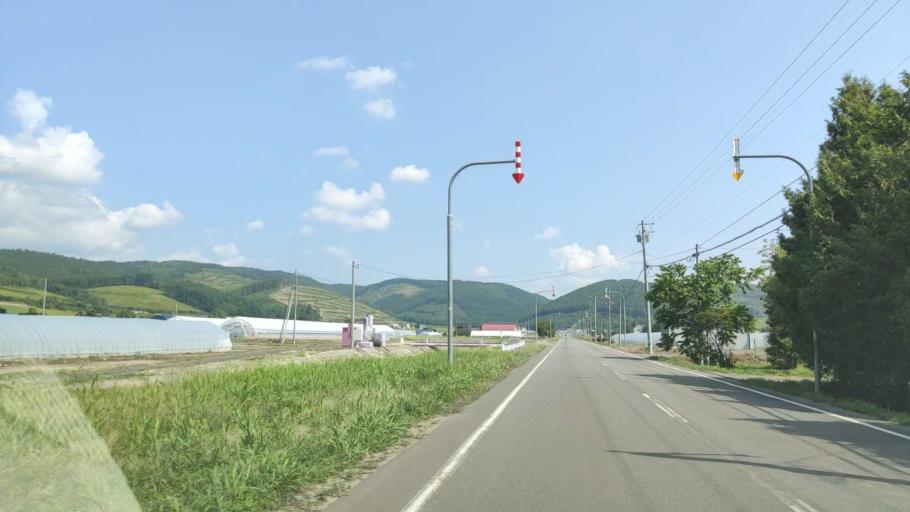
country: JP
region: Hokkaido
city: Shimo-furano
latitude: 43.4089
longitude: 142.3970
